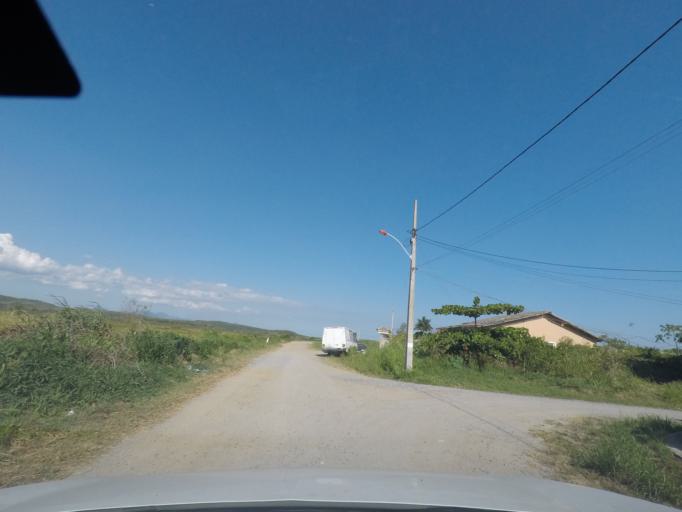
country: BR
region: Rio de Janeiro
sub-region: Marica
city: Marica
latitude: -22.9644
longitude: -42.9227
